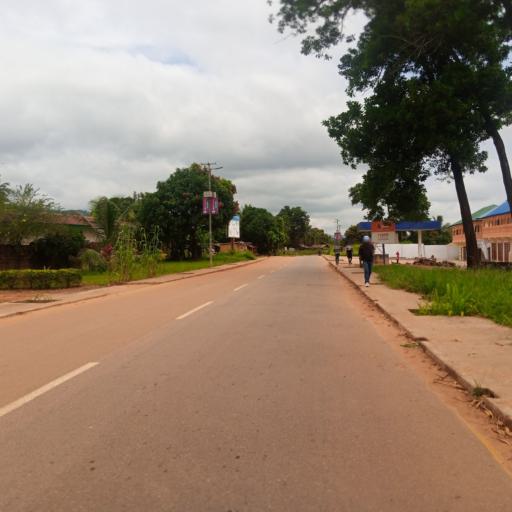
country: SL
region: Eastern Province
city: Kenema
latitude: 7.8572
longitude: -11.2041
